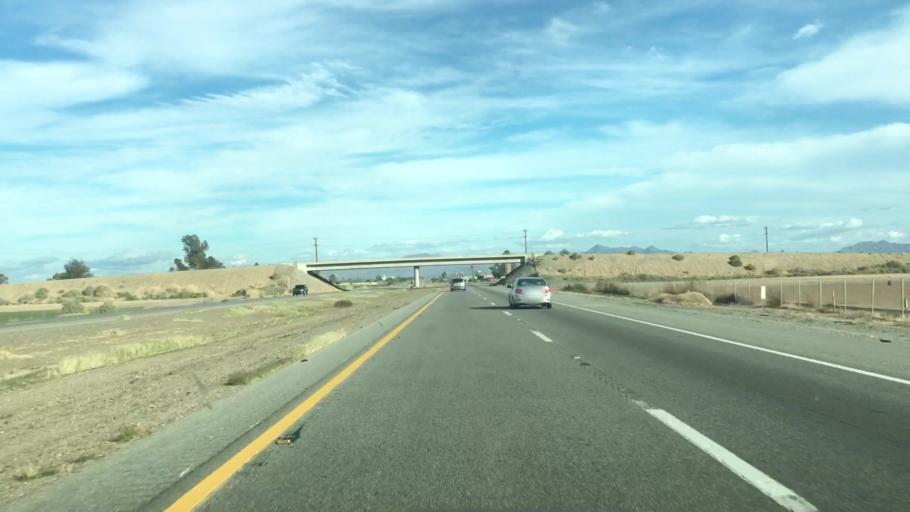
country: US
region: California
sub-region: Riverside County
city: Blythe
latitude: 33.6065
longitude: -114.6255
